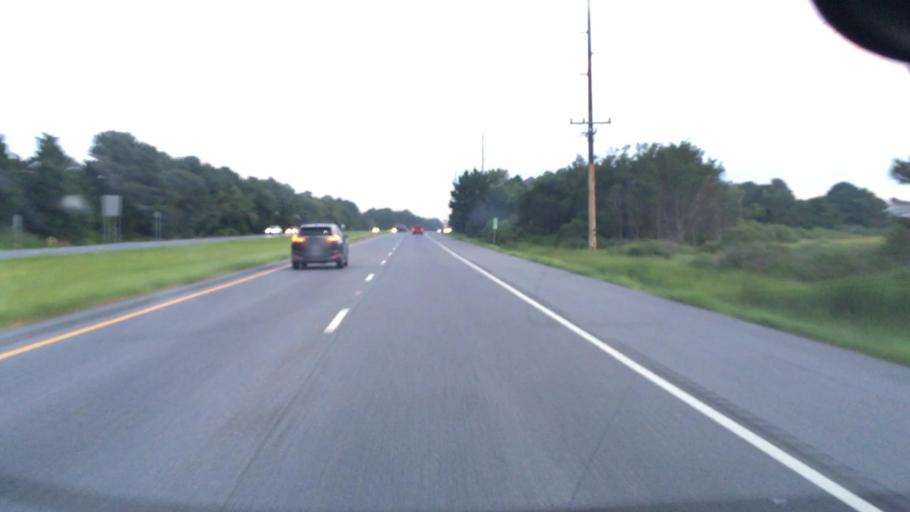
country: US
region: Delaware
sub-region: Sussex County
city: Bethany Beach
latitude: 38.5803
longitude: -75.0613
